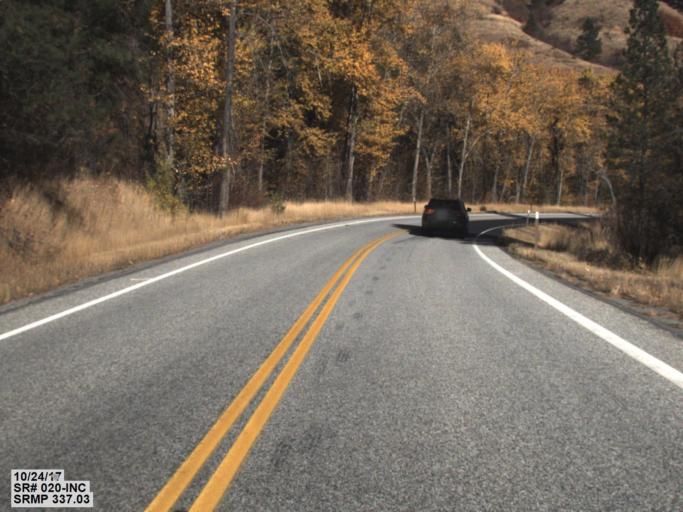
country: US
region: Washington
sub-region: Stevens County
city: Kettle Falls
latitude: 48.5911
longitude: -118.1877
